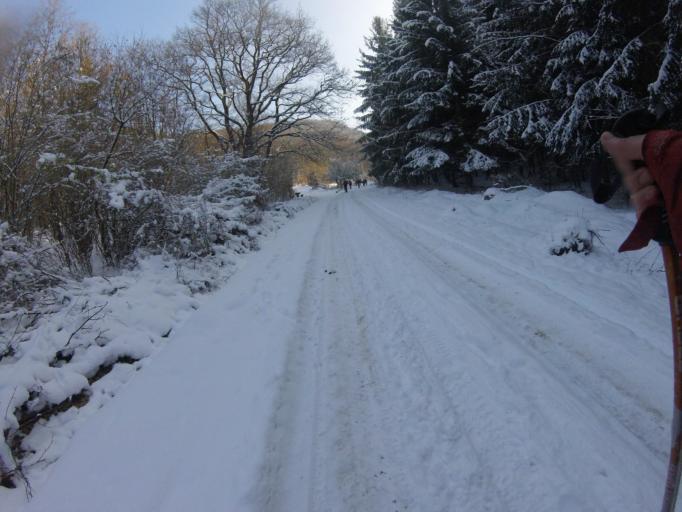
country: HU
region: Heves
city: Belapatfalva
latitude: 48.0610
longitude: 20.3790
